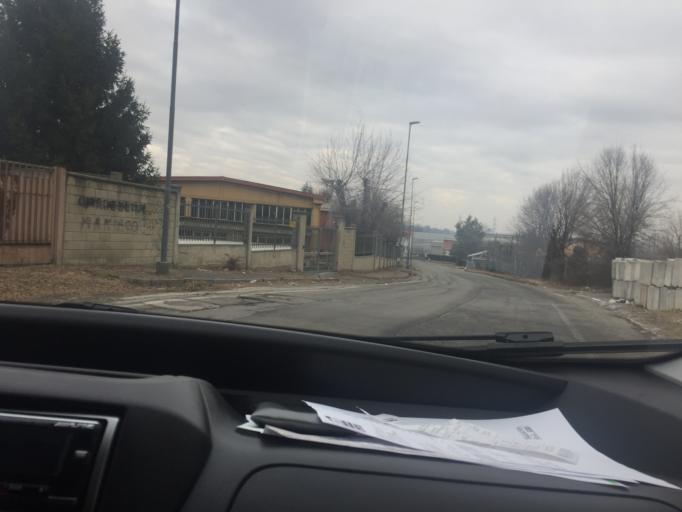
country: IT
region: Piedmont
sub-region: Provincia di Torino
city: Savonera
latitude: 45.0875
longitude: 7.6125
